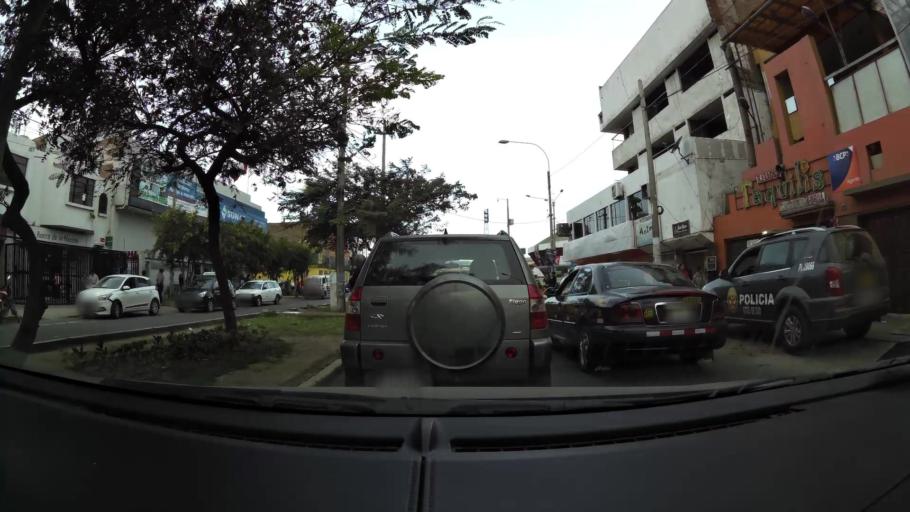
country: PE
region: La Libertad
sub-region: Provincia de Trujillo
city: Trujillo
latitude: -8.1036
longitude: -79.0320
